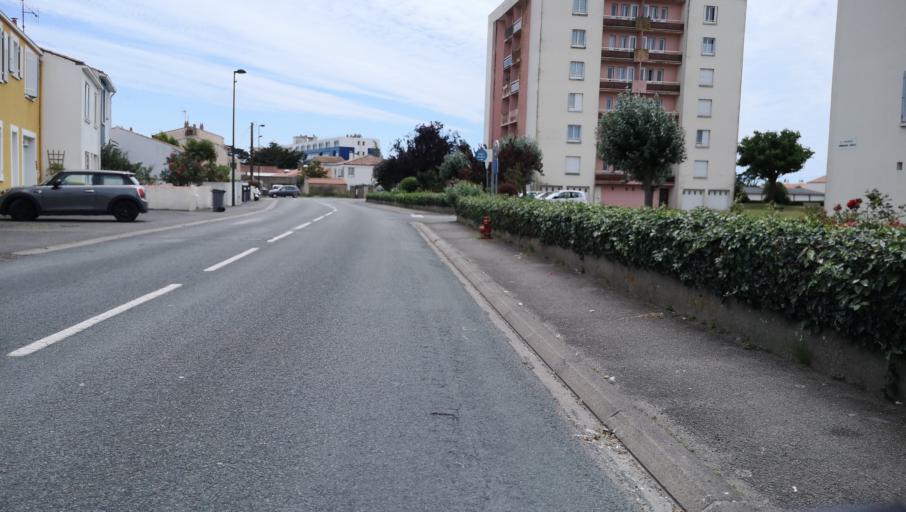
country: FR
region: Pays de la Loire
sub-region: Departement de la Vendee
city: Les Sables-d'Olonne
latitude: 46.5074
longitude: -1.7741
